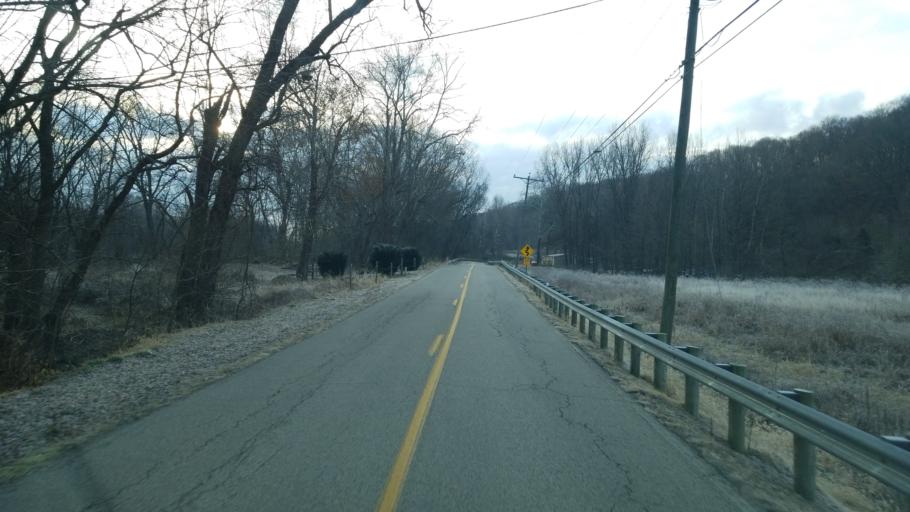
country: US
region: Ohio
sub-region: Ross County
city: Chillicothe
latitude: 39.2598
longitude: -82.9149
